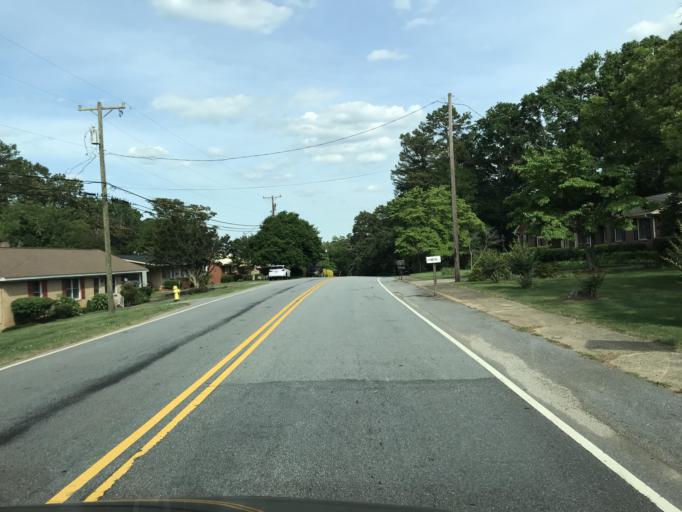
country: US
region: South Carolina
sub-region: Greenville County
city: Gantt
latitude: 34.7992
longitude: -82.3958
